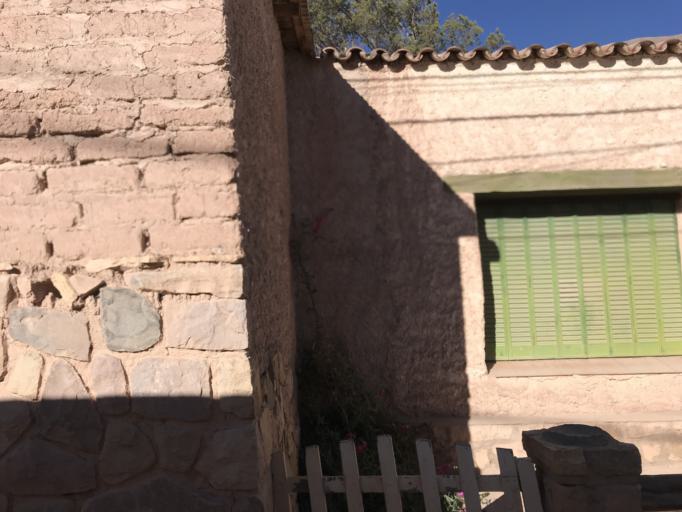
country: AR
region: Jujuy
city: Maimara
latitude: -23.6252
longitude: -65.4082
